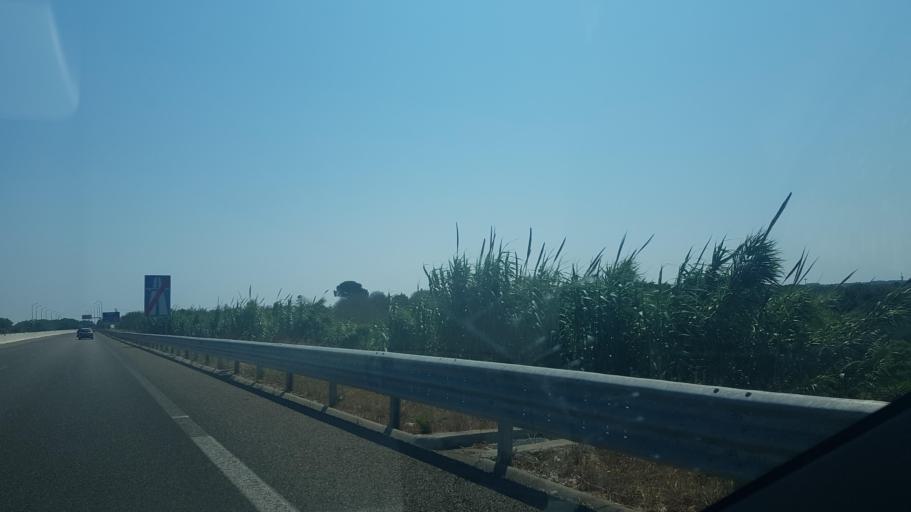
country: IT
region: Apulia
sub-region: Provincia di Lecce
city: Otranto
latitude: 40.1470
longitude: 18.4690
